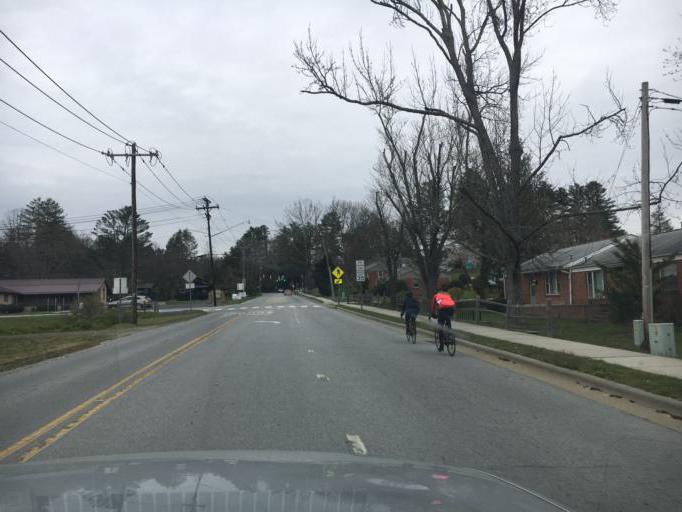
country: US
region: North Carolina
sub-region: Transylvania County
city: Brevard
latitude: 35.2256
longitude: -82.7244
